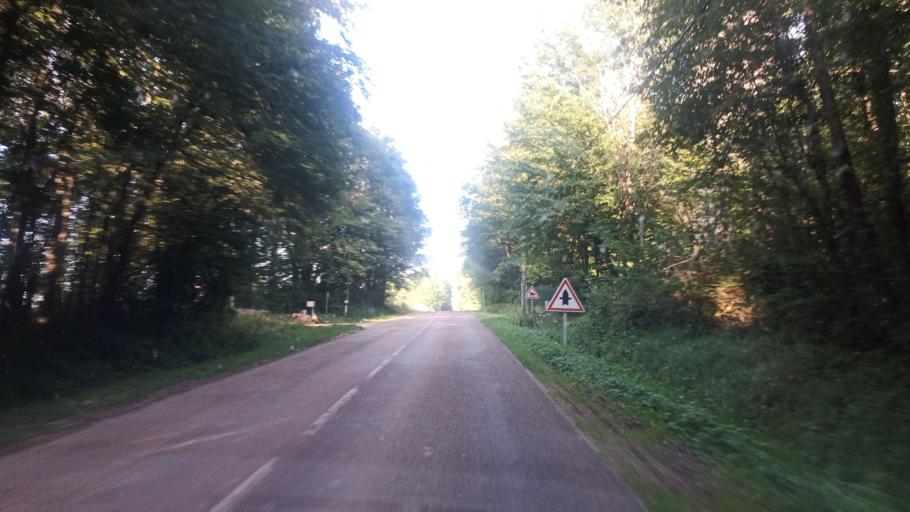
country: FR
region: Bourgogne
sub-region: Departement de l'Yonne
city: Saint-Valerien
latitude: 48.2382
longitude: 3.1364
